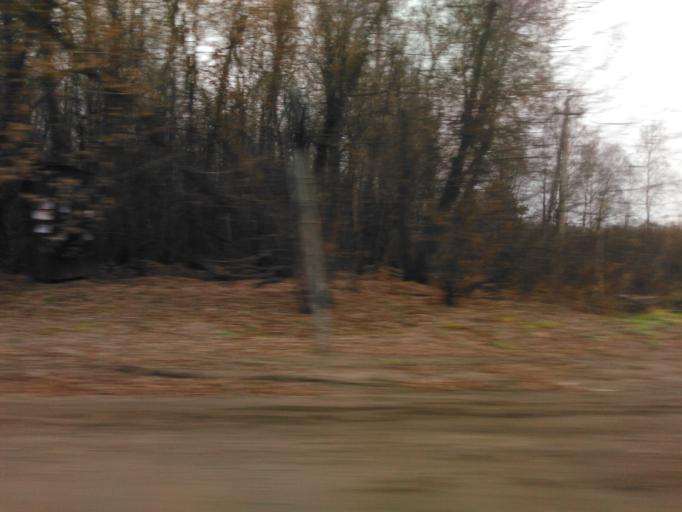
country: RU
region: Moskovskaya
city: Ashukino
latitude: 56.1445
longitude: 37.9882
